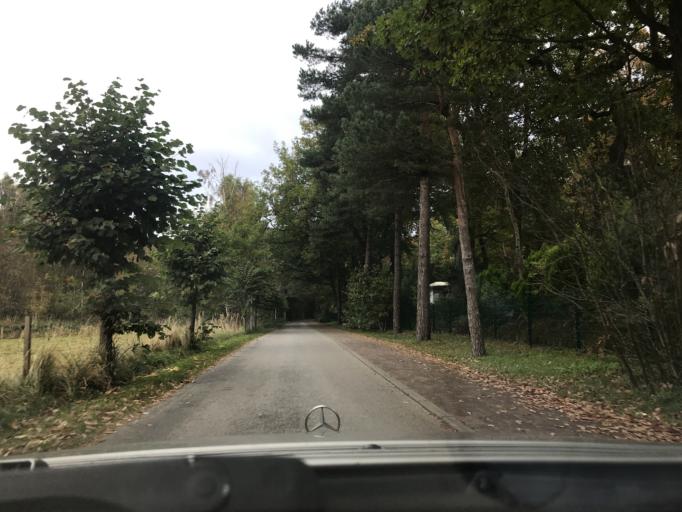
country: DE
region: Mecklenburg-Vorpommern
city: Loddin
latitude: 54.0325
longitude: 14.0381
